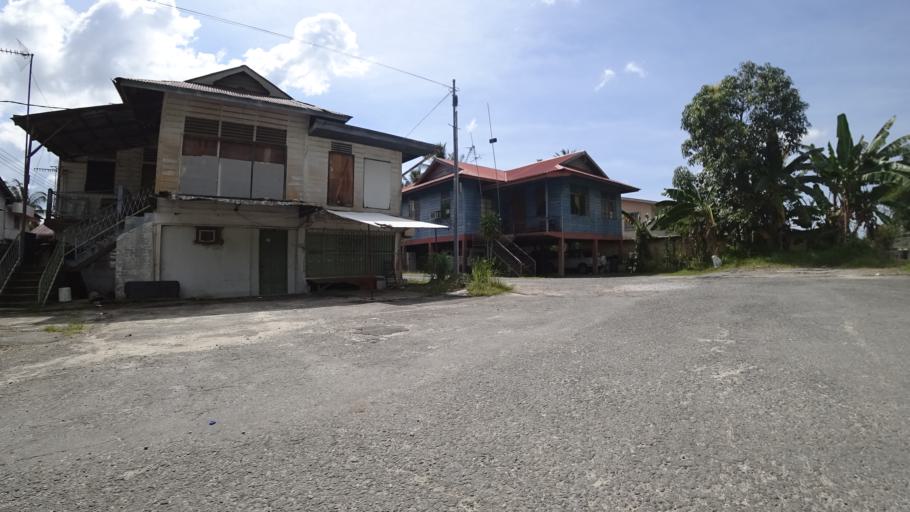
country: BN
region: Brunei and Muara
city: Bandar Seri Begawan
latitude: 4.8540
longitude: 114.8731
